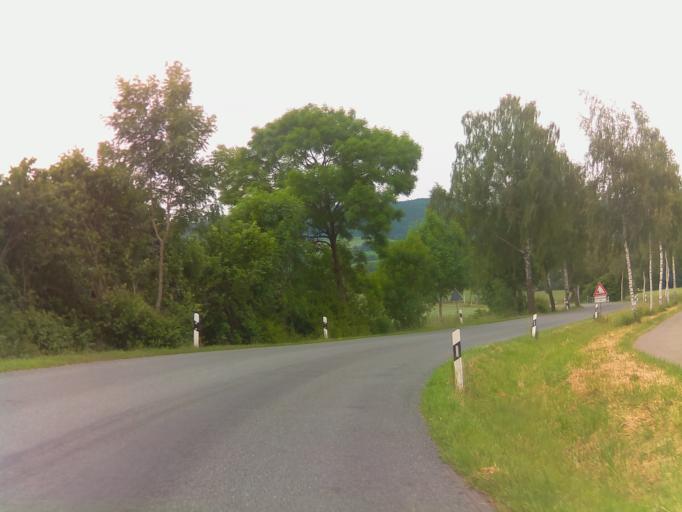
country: DE
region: North Rhine-Westphalia
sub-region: Regierungsbezirk Detmold
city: Schieder-Schwalenberg
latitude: 51.8458
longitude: 9.2802
